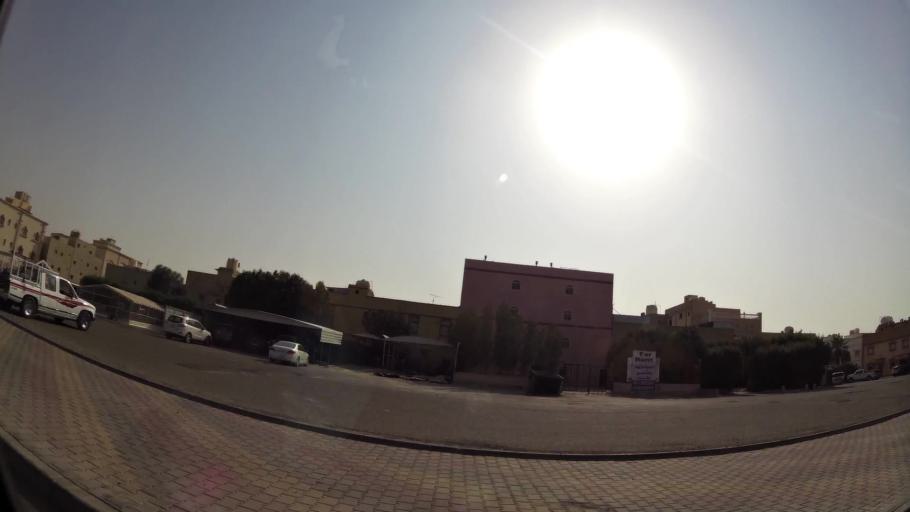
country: KW
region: Muhafazat al Jahra'
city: Al Jahra'
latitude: 29.3506
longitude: 47.6895
